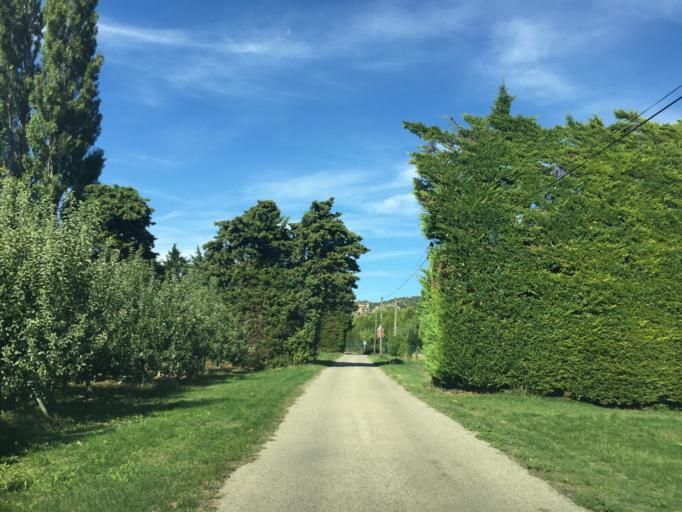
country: FR
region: Provence-Alpes-Cote d'Azur
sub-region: Departement du Vaucluse
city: Mornas
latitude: 44.1925
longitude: 4.7303
